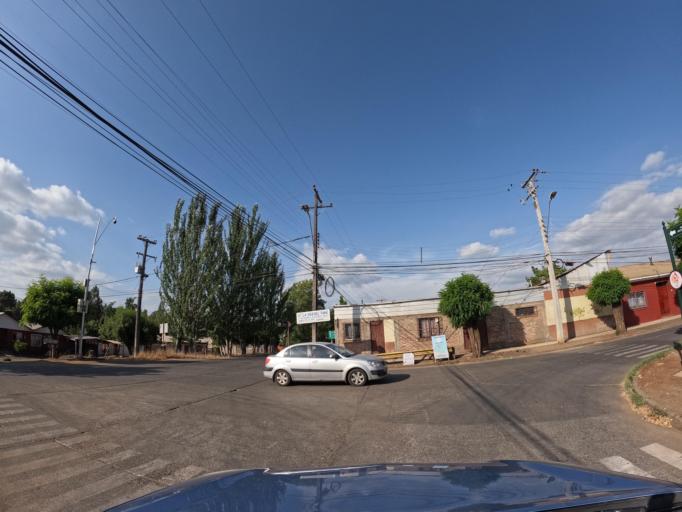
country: CL
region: Maule
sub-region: Provincia de Curico
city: Molina
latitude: -35.2791
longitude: -71.2575
